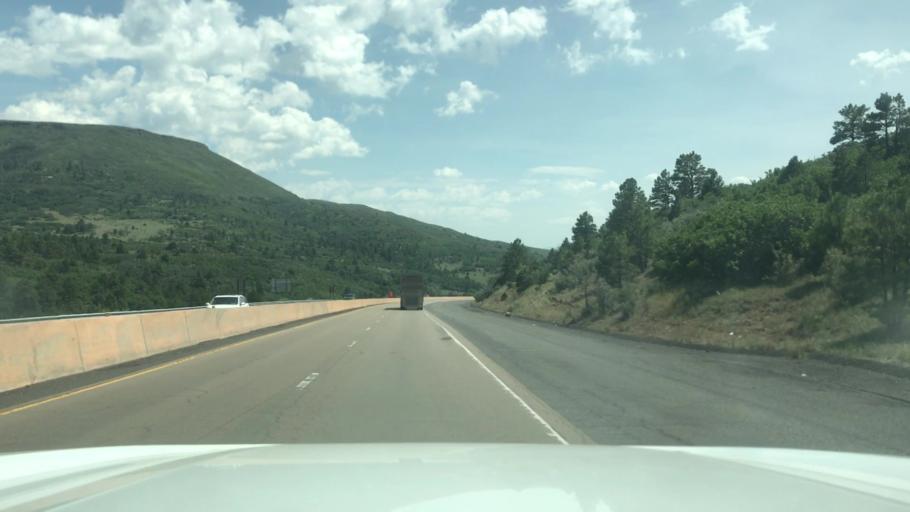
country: US
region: New Mexico
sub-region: Colfax County
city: Raton
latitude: 36.9773
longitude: -104.4806
